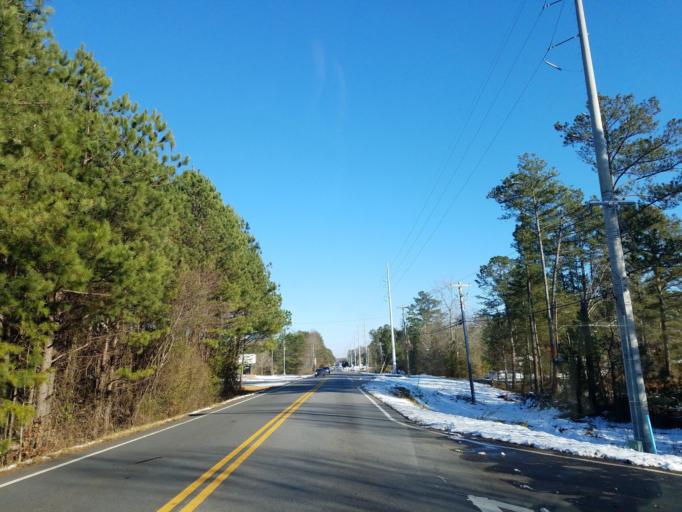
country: US
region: Georgia
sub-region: Dawson County
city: Dawsonville
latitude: 34.3538
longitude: -84.0809
